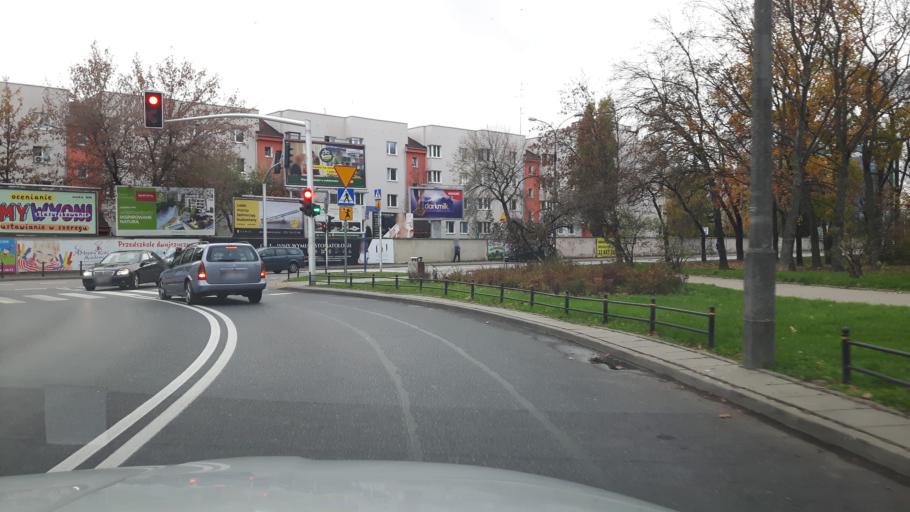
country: PL
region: Masovian Voivodeship
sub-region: Warszawa
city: Mokotow
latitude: 52.1694
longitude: 21.0001
